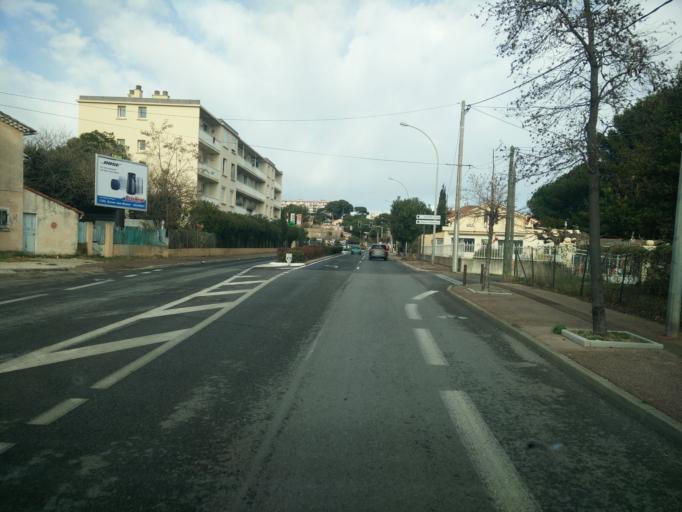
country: FR
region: Provence-Alpes-Cote d'Azur
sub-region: Departement du Var
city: La Seyne-sur-Mer
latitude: 43.0840
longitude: 5.8816
